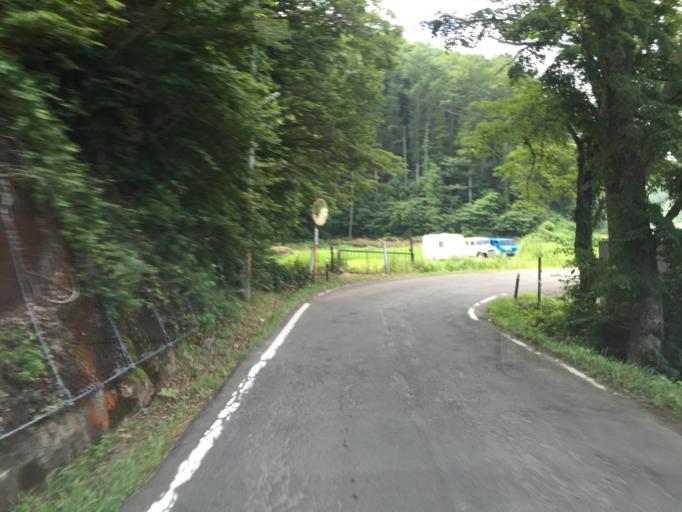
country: JP
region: Fukushima
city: Inawashiro
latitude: 37.4131
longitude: 140.1124
